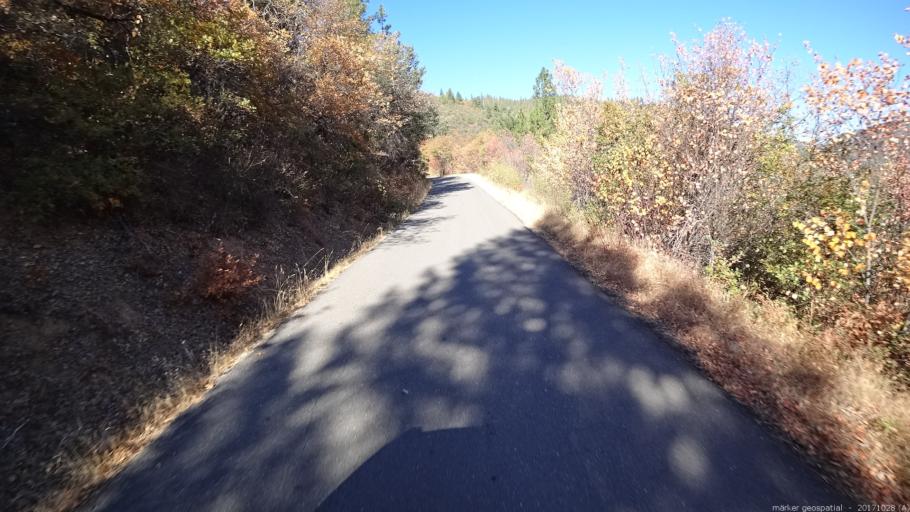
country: US
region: California
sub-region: Trinity County
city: Lewiston
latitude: 40.7977
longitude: -122.6114
